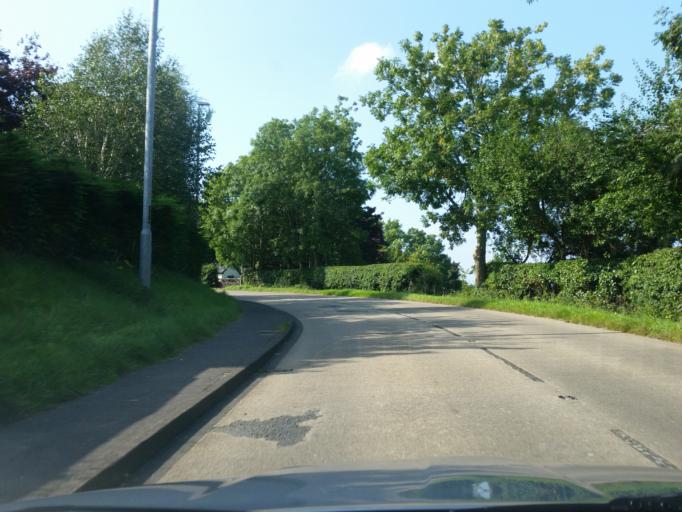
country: GB
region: Northern Ireland
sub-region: Fermanagh District
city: Enniskillen
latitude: 54.3552
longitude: -7.6222
